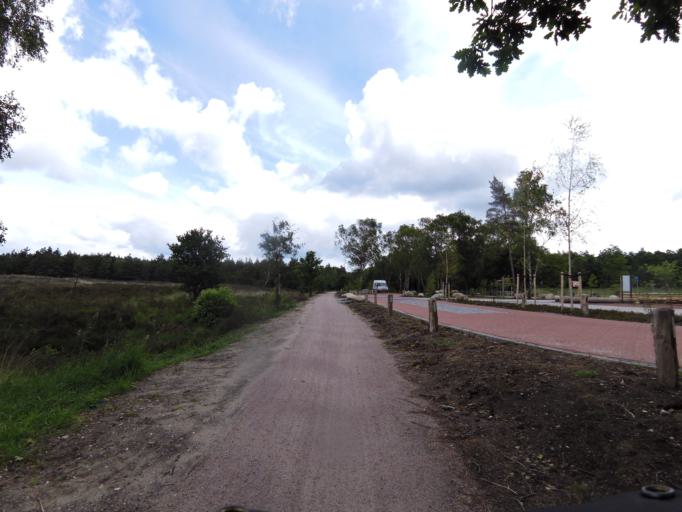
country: NL
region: Gelderland
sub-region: Gemeente Nunspeet
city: Nunspeet
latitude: 52.3301
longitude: 5.7736
